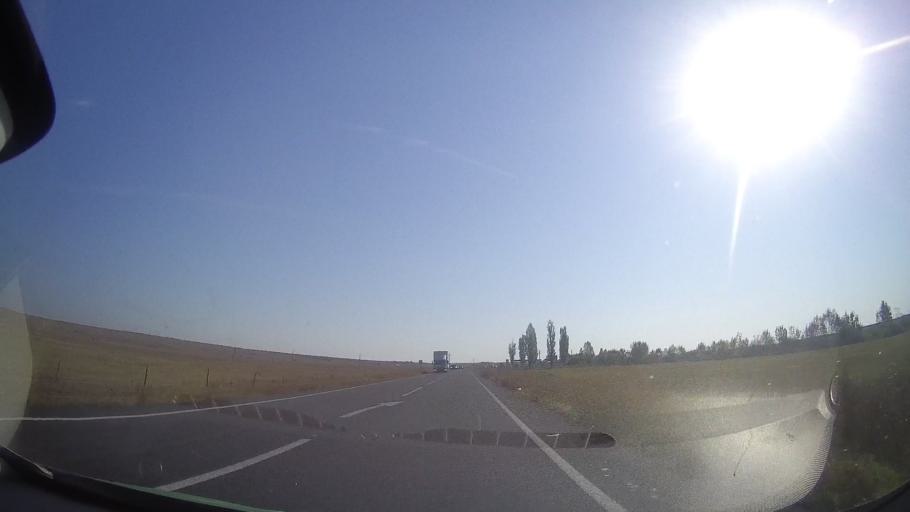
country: RO
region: Timis
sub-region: Comuna Topolovatu Mare
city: Topolovatu Mare
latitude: 45.7839
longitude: 21.5957
